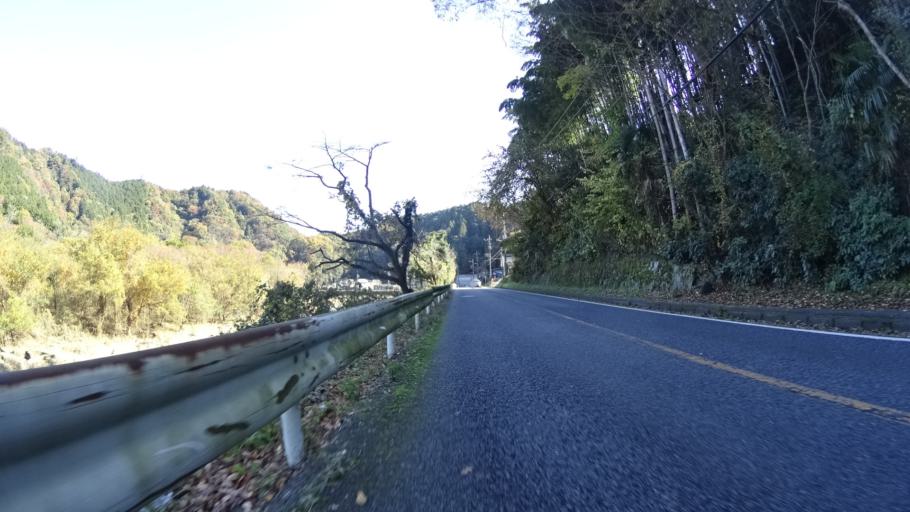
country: JP
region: Kanagawa
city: Zama
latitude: 35.5364
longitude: 139.2785
